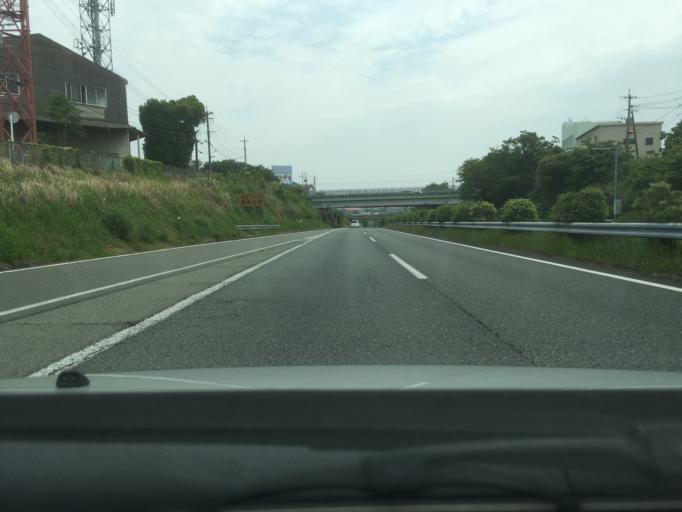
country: JP
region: Kumamoto
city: Kumamoto
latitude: 32.8494
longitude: 130.7667
